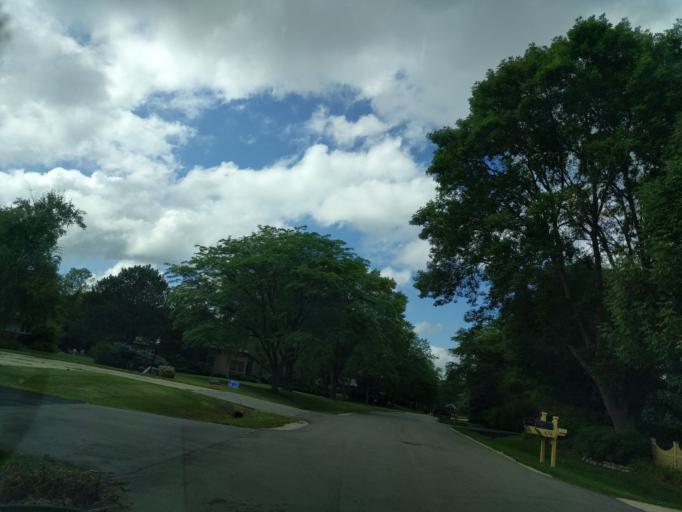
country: US
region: Wisconsin
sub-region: Milwaukee County
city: Bayside
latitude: 43.1866
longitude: -87.9002
